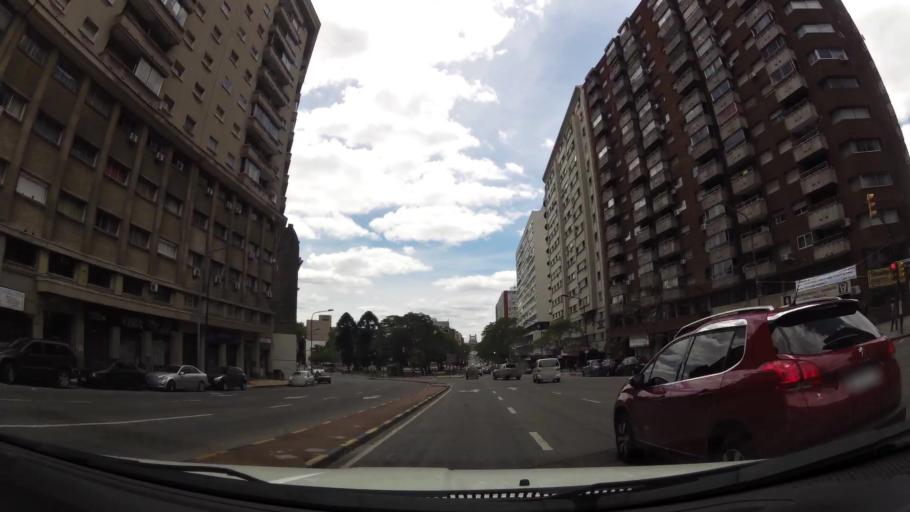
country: UY
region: Montevideo
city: Montevideo
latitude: -34.9012
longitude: -56.1920
